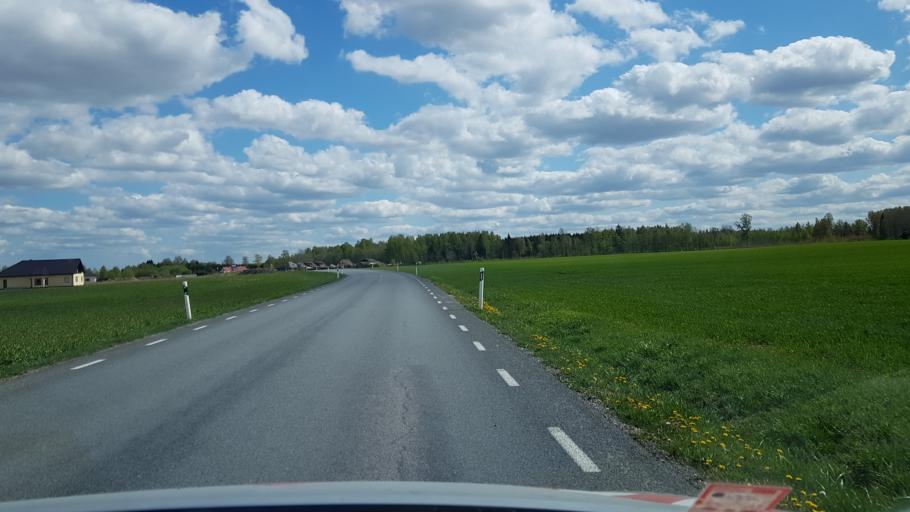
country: EE
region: Tartu
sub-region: UElenurme vald
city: Ulenurme
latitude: 58.3152
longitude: 26.6430
